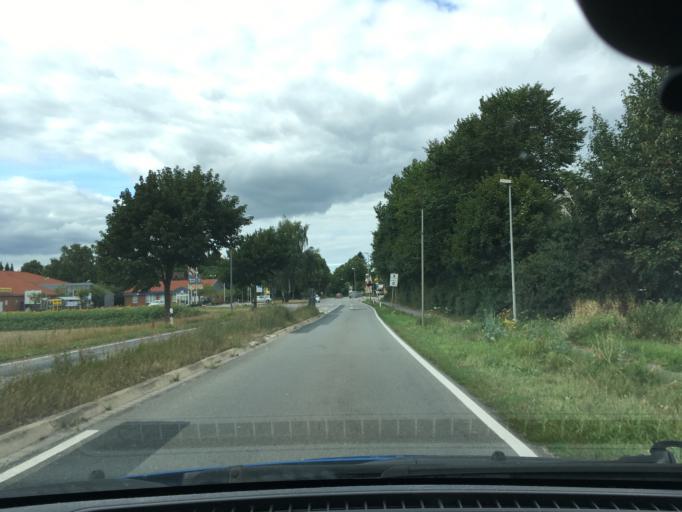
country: DE
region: Lower Saxony
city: Neu Wulmstorf
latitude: 53.4215
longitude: 9.7897
